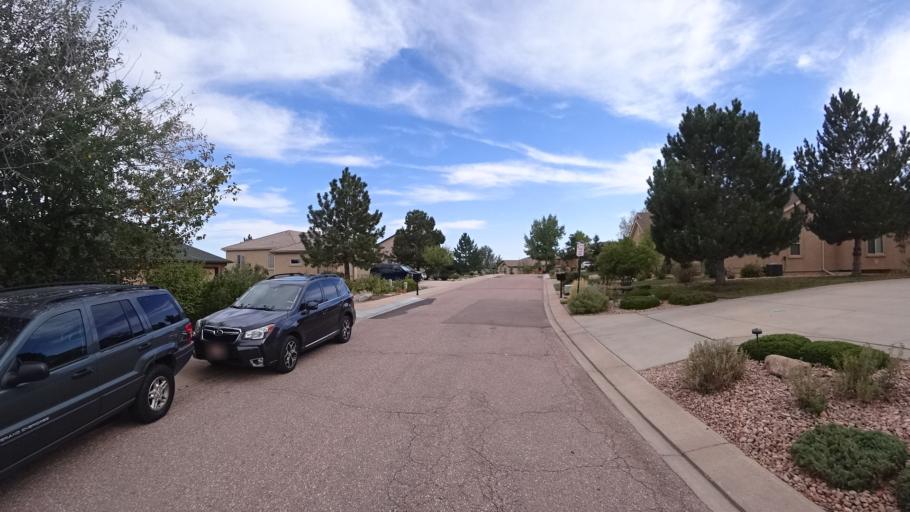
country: US
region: Colorado
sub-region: El Paso County
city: Colorado Springs
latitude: 38.8987
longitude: -104.7871
